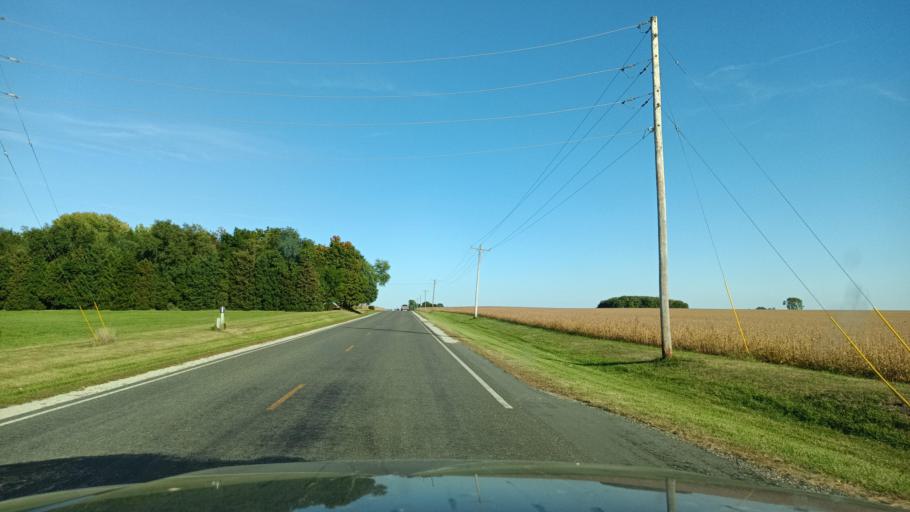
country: US
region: Illinois
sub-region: De Witt County
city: Clinton
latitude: 40.2244
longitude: -88.9170
